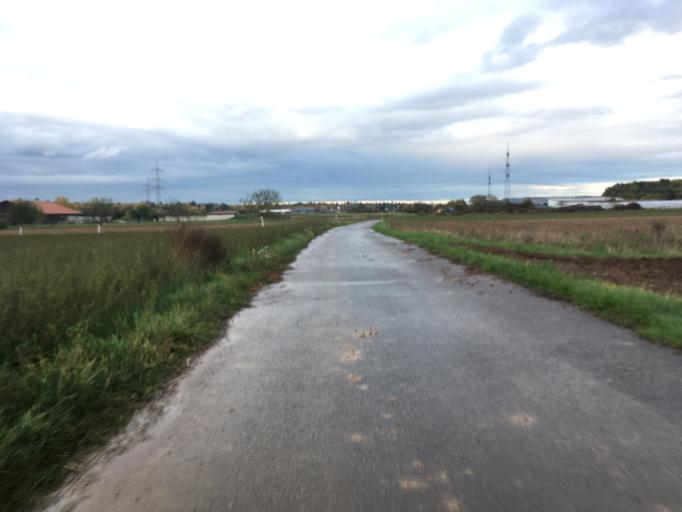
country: DE
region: Baden-Wuerttemberg
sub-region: Regierungsbezirk Stuttgart
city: Nordheim
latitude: 49.1032
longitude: 9.1574
